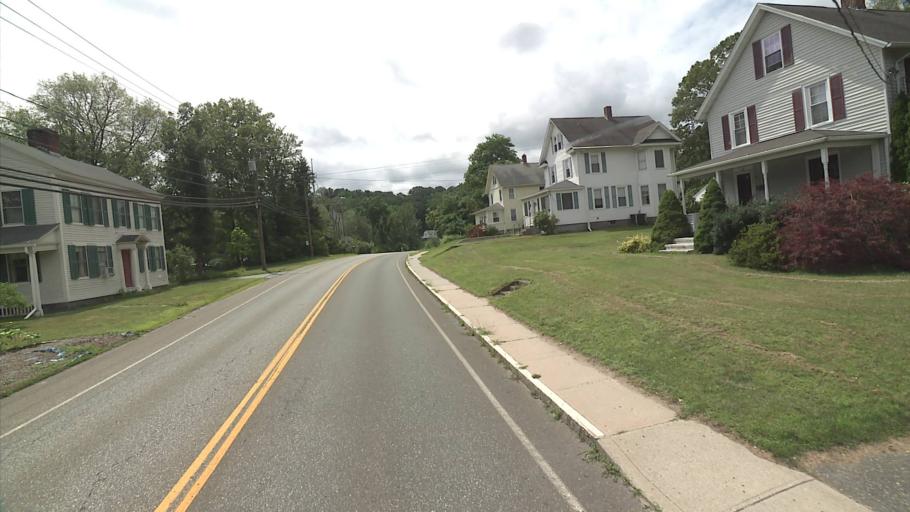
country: US
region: Connecticut
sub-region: Middlesex County
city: Deep River Center
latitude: 41.3820
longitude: -72.4395
